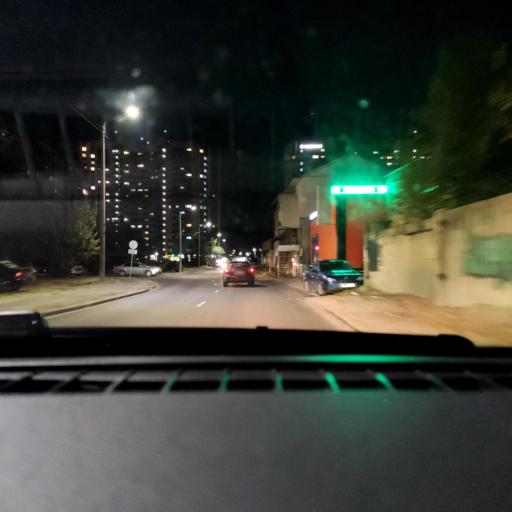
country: RU
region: Voronezj
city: Maslovka
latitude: 51.5910
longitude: 39.2436
